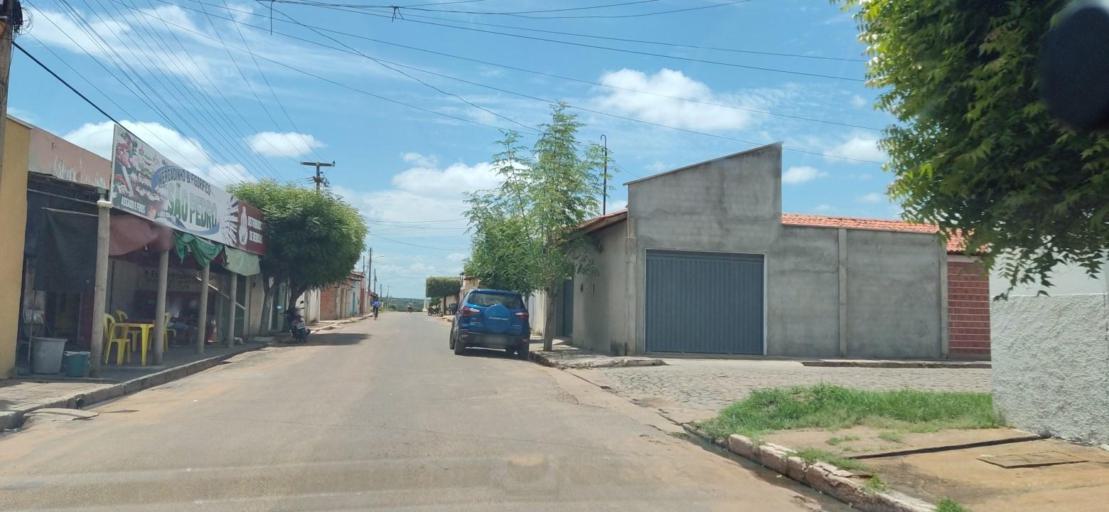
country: BR
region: Piaui
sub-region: Valenca Do Piaui
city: Valenca do Piaui
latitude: -6.4084
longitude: -41.7326
